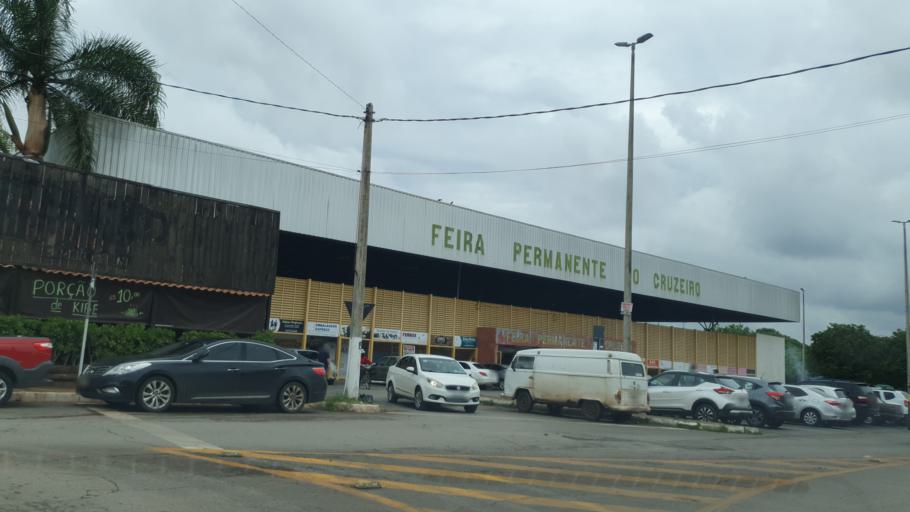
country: BR
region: Federal District
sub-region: Brasilia
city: Brasilia
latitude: -15.7915
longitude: -47.9376
